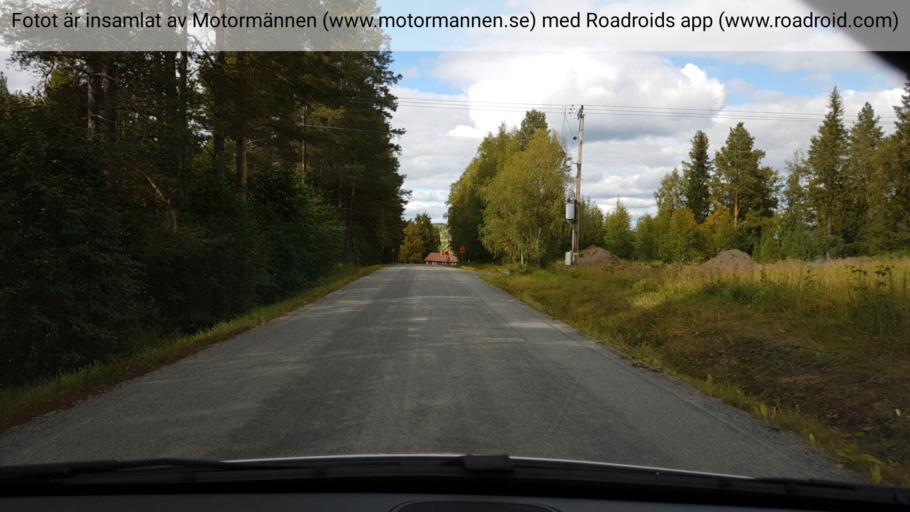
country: SE
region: Jaemtland
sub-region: OEstersunds Kommun
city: Ostersund
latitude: 63.1470
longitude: 14.5464
